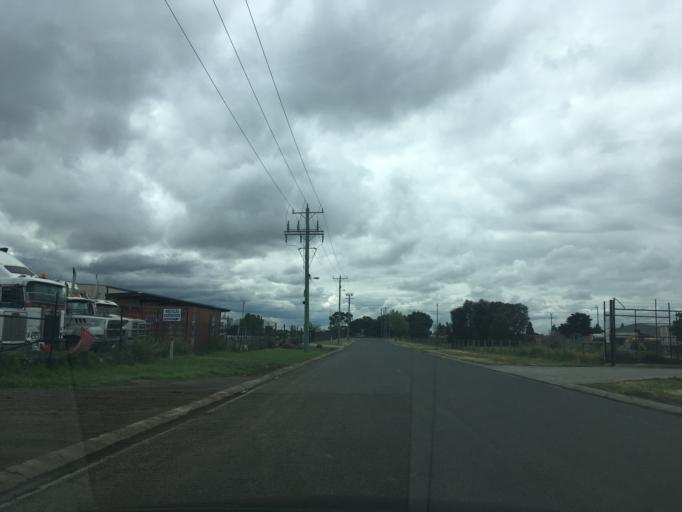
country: AU
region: Victoria
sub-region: Brimbank
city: Sunshine West
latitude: -37.8167
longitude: 144.7951
